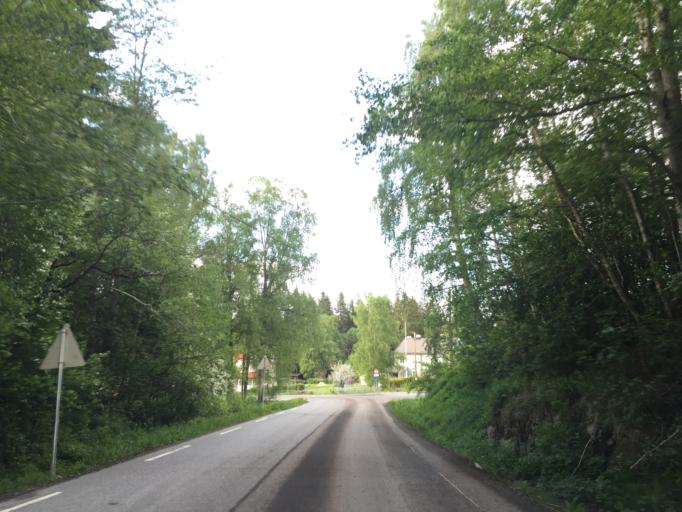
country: NO
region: Akershus
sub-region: Nes
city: Auli
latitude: 60.0248
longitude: 11.3295
